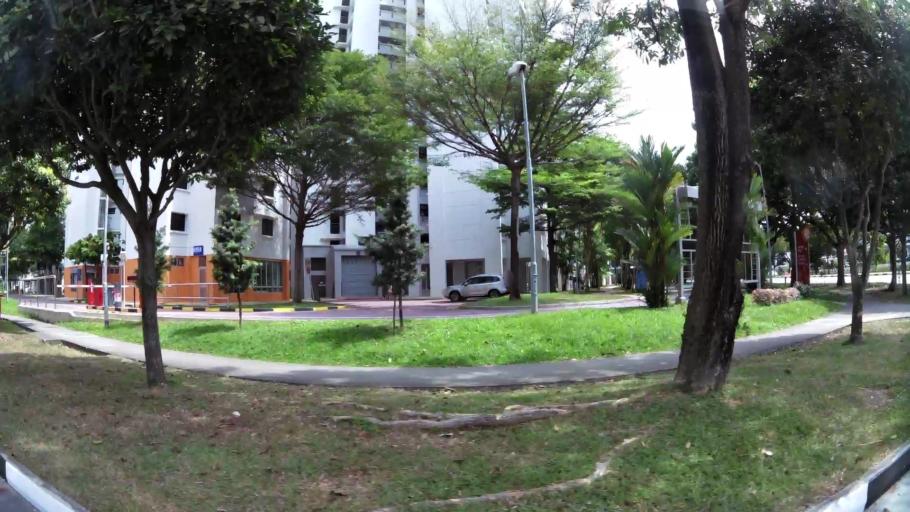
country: MY
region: Johor
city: Johor Bahru
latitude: 1.3351
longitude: 103.6991
